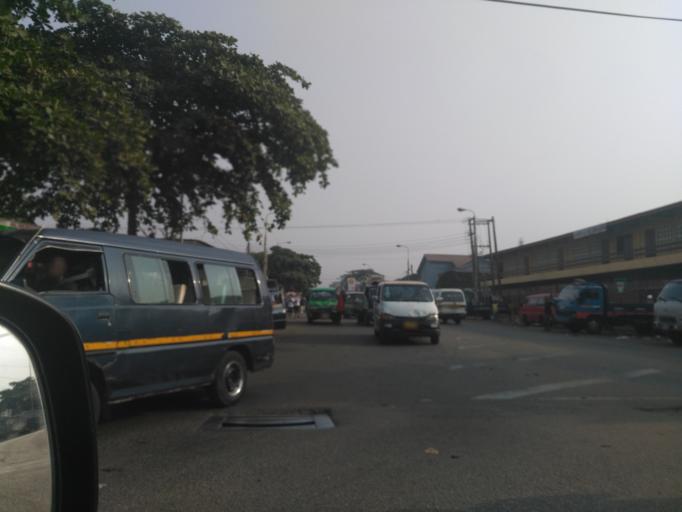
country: GH
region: Greater Accra
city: Accra
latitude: 5.5780
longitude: -0.2007
